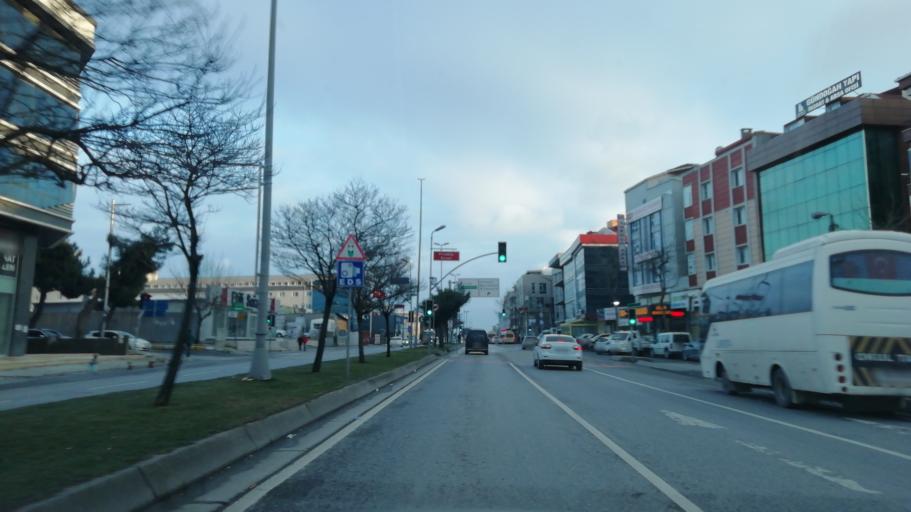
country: TR
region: Istanbul
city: Esenyurt
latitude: 41.0079
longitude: 28.7038
